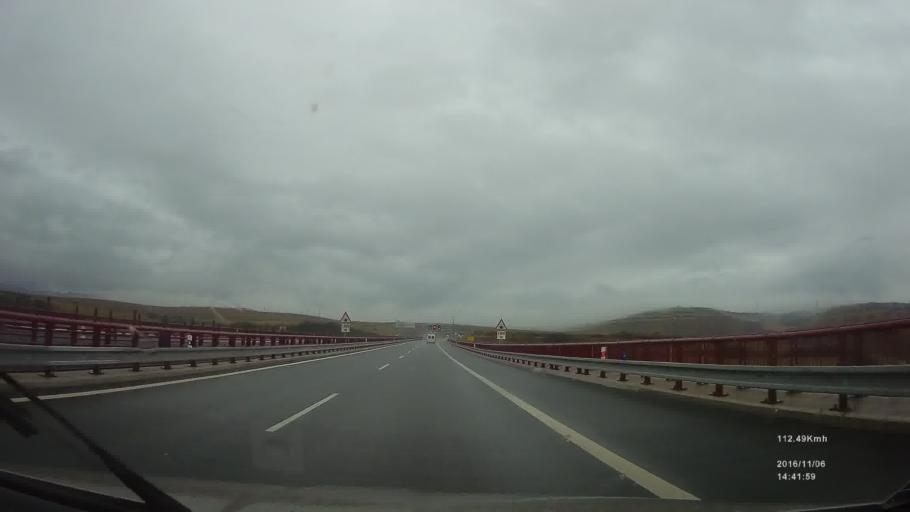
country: SK
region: Presovsky
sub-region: Okres Presov
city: Levoca
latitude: 49.0075
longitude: 20.5924
